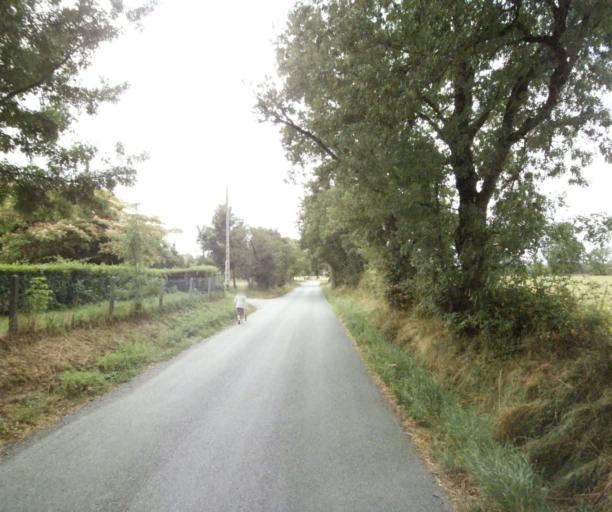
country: FR
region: Midi-Pyrenees
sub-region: Departement du Tarn
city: Soreze
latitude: 43.4583
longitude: 2.0589
